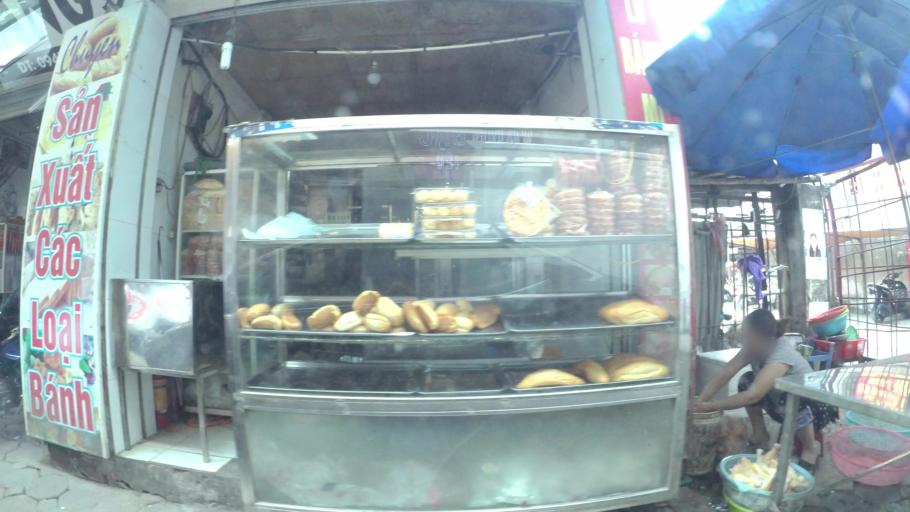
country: VN
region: Ha Noi
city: Thanh Xuan
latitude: 20.9925
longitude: 105.8174
